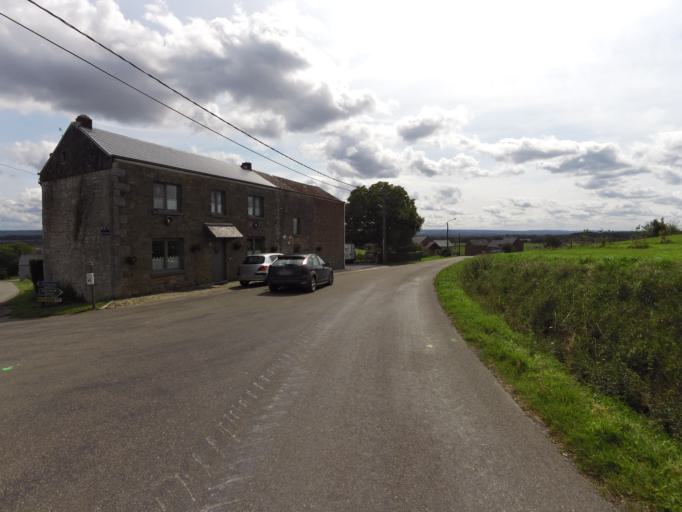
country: BE
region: Wallonia
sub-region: Province du Luxembourg
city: Durbuy
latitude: 50.3637
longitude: 5.4301
